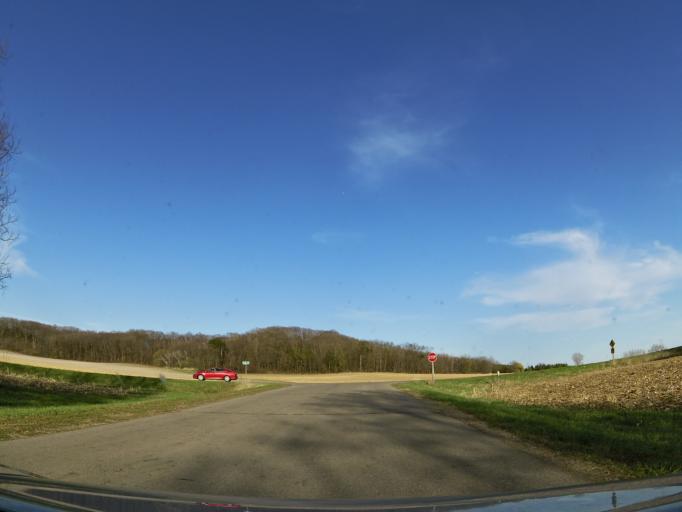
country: US
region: Minnesota
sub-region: Washington County
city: Afton
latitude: 44.8454
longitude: -92.7168
